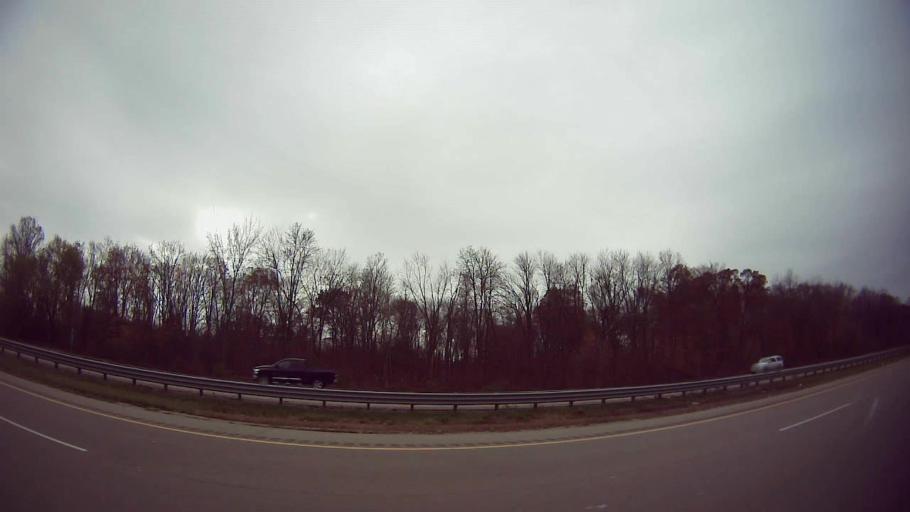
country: US
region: Michigan
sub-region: Oakland County
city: Clarkston
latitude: 42.7465
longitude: -83.4114
